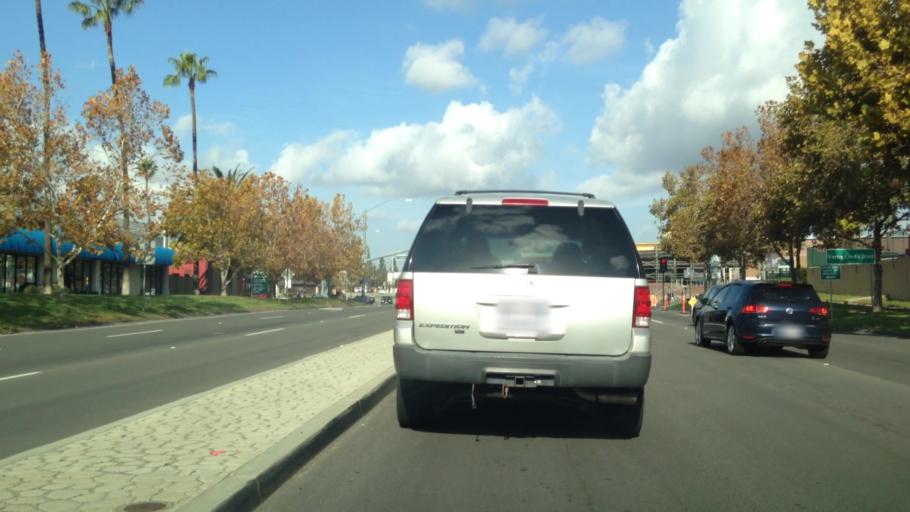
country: US
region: California
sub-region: Orange County
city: Yorba Linda
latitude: 33.8876
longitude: -117.8128
